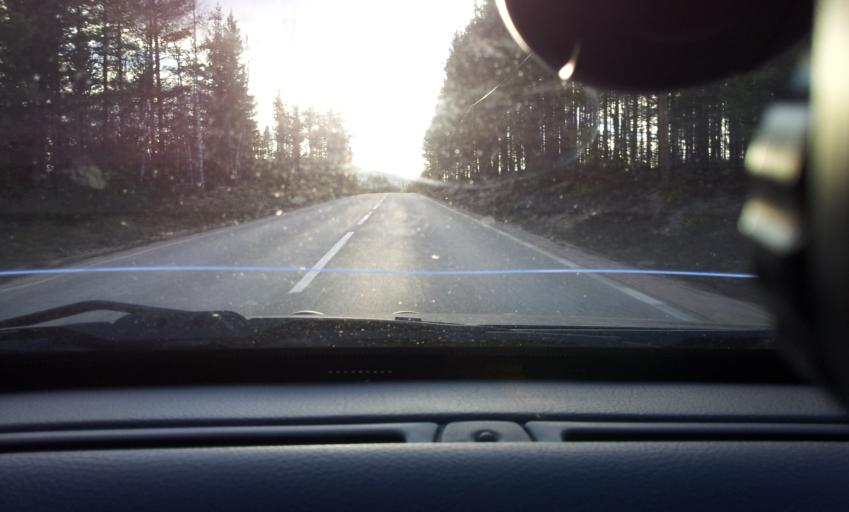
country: SE
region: Jaemtland
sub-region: Harjedalens Kommun
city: Sveg
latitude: 62.1240
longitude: 15.0005
